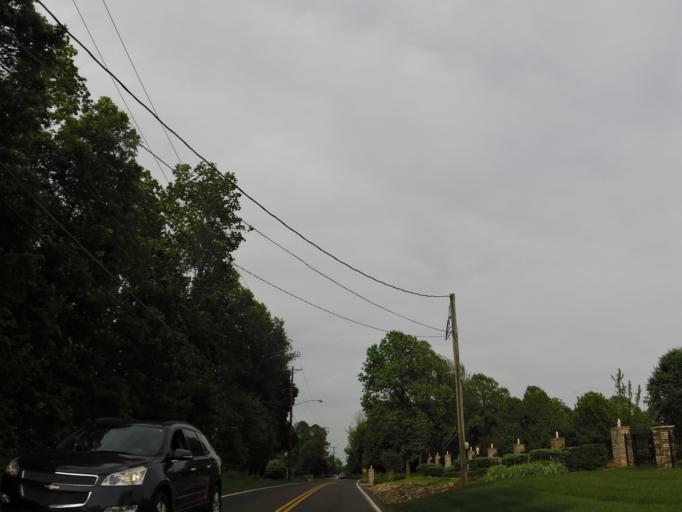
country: US
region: Tennessee
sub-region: Knox County
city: Knoxville
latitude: 36.0250
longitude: -83.8709
